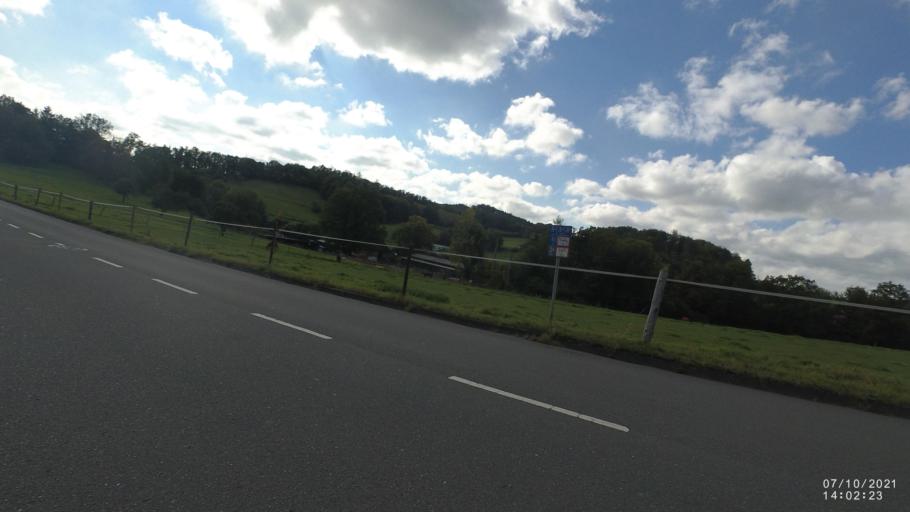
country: DE
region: North Rhine-Westphalia
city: Hemer
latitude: 51.4011
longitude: 7.7578
